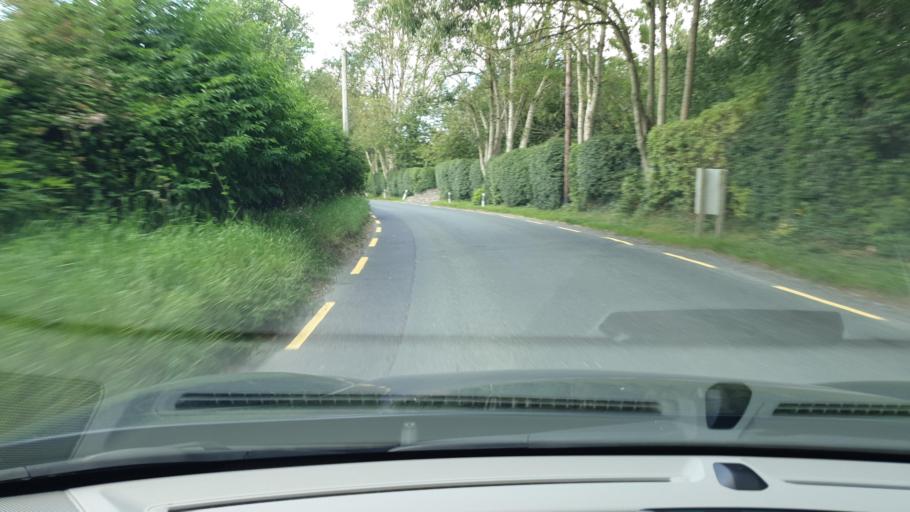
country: IE
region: Leinster
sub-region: An Mhi
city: Dunshaughlin
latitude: 53.5468
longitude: -6.6268
